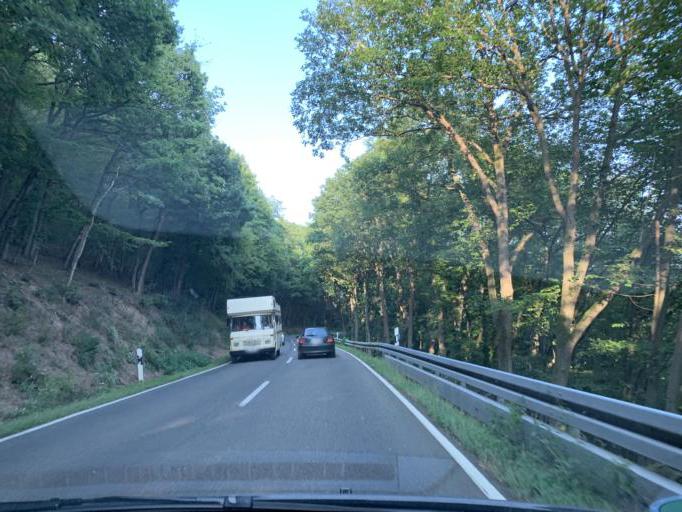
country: DE
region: North Rhine-Westphalia
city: Heimbach
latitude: 50.6422
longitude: 6.4553
